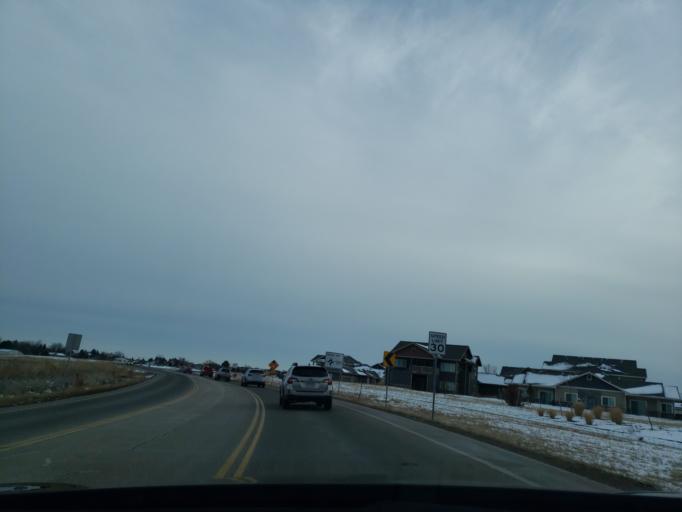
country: US
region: Colorado
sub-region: Larimer County
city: Campion
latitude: 40.3483
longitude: -105.0971
